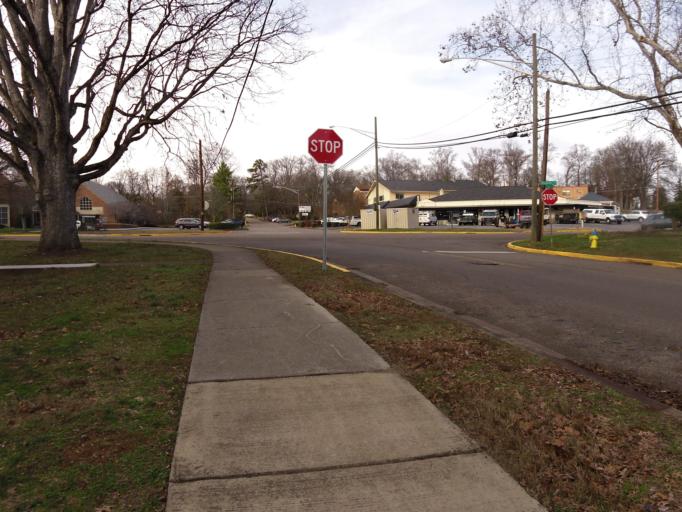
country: US
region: Tennessee
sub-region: Knox County
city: Knoxville
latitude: 35.9333
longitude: -83.9637
